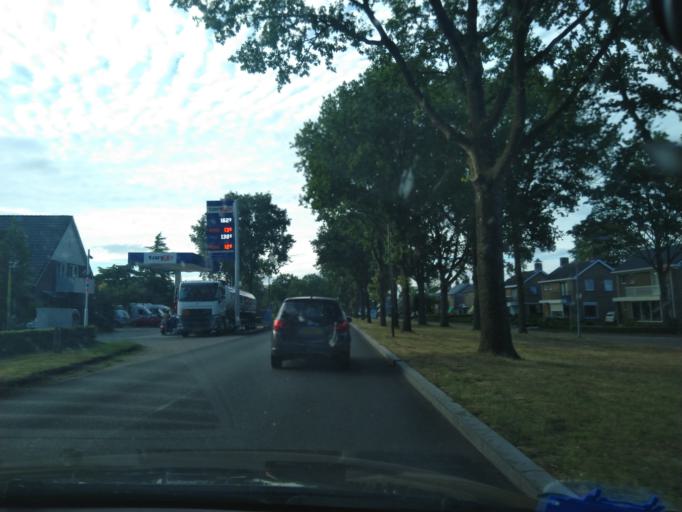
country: NL
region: Drenthe
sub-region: Gemeente Aa en Hunze
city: Anloo
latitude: 52.9821
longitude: 6.6491
